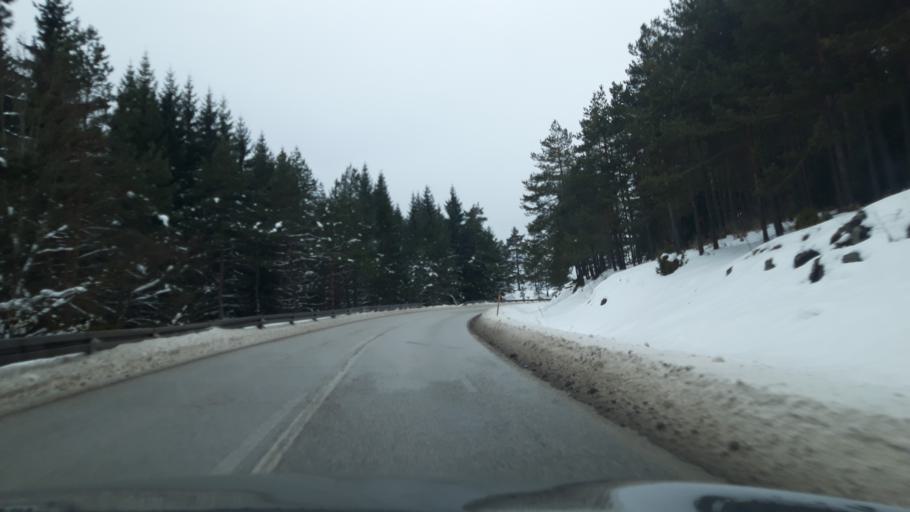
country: BA
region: Republika Srpska
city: Sokolac
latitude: 43.9079
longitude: 18.7114
